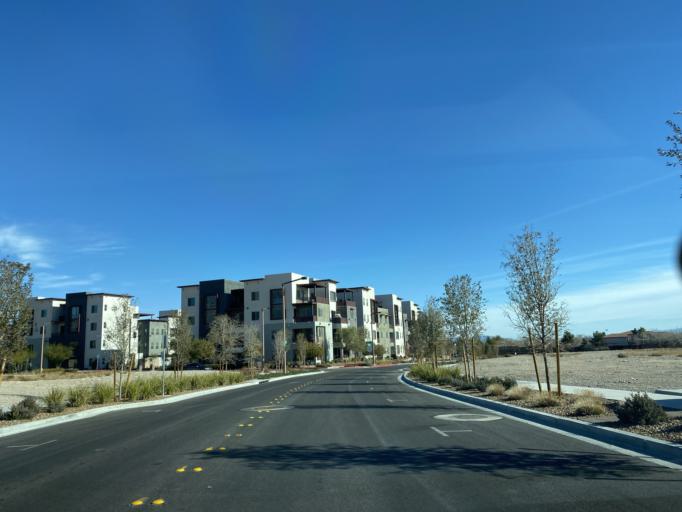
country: US
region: Nevada
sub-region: Clark County
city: Summerlin South
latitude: 36.1550
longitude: -115.3255
